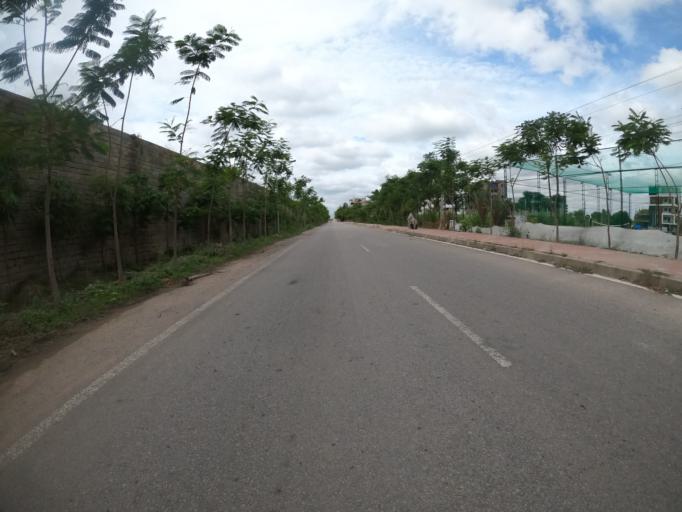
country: IN
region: Telangana
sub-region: Rangareddi
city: Sriramnagar
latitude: 17.2673
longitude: 78.3781
